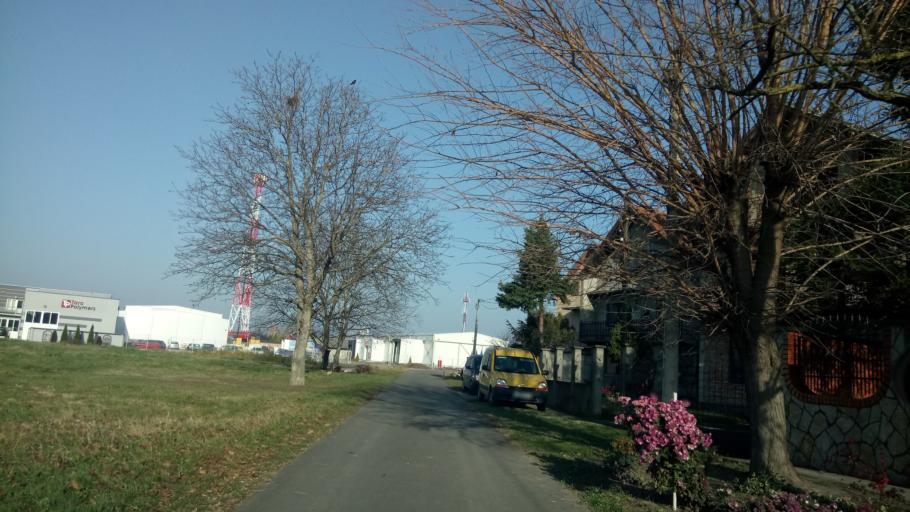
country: RS
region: Autonomna Pokrajina Vojvodina
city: Nova Pazova
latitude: 44.9491
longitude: 20.2077
